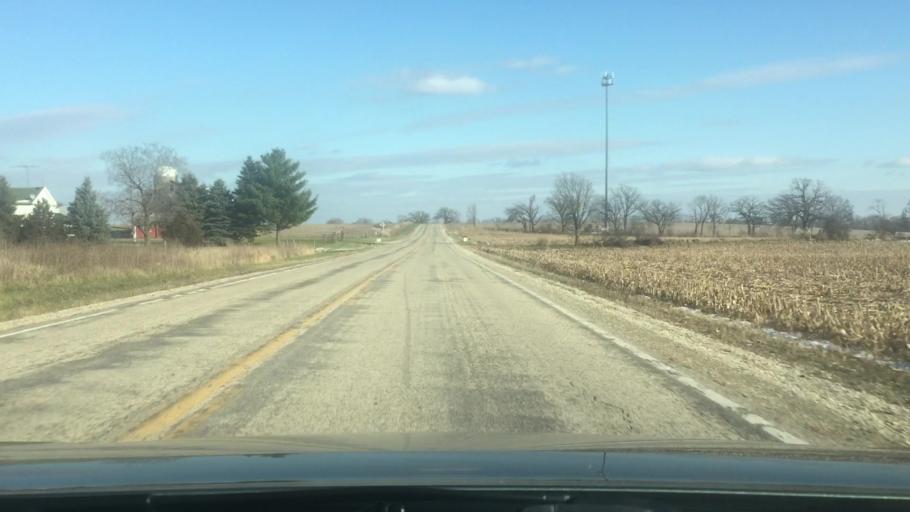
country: US
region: Wisconsin
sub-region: Jefferson County
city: Palmyra
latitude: 42.9262
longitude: -88.5582
